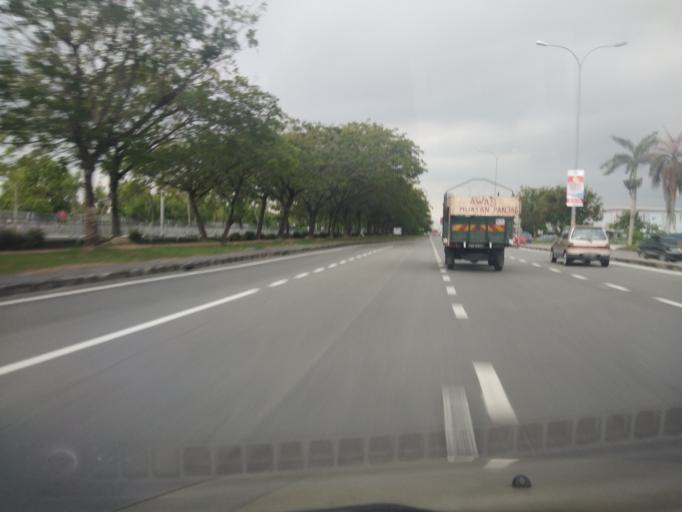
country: MY
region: Penang
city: Tasek Glugor
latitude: 5.5198
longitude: 100.4759
